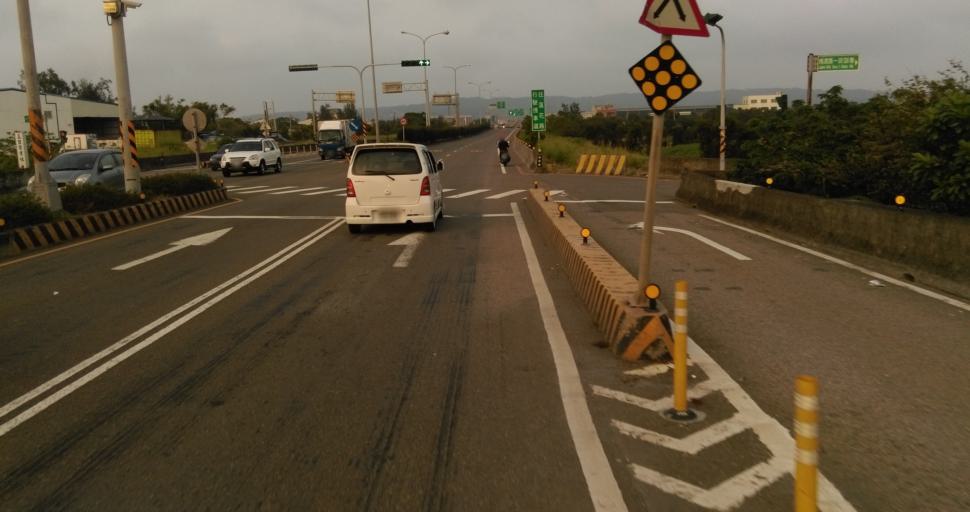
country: TW
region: Taiwan
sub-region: Hsinchu
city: Hsinchu
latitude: 24.8525
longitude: 120.9434
